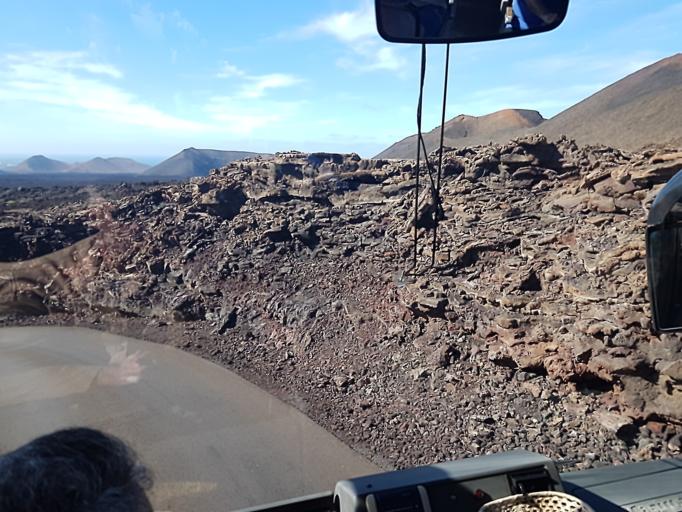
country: ES
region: Canary Islands
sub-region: Provincia de Las Palmas
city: Yaiza
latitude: 28.9960
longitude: -13.7582
